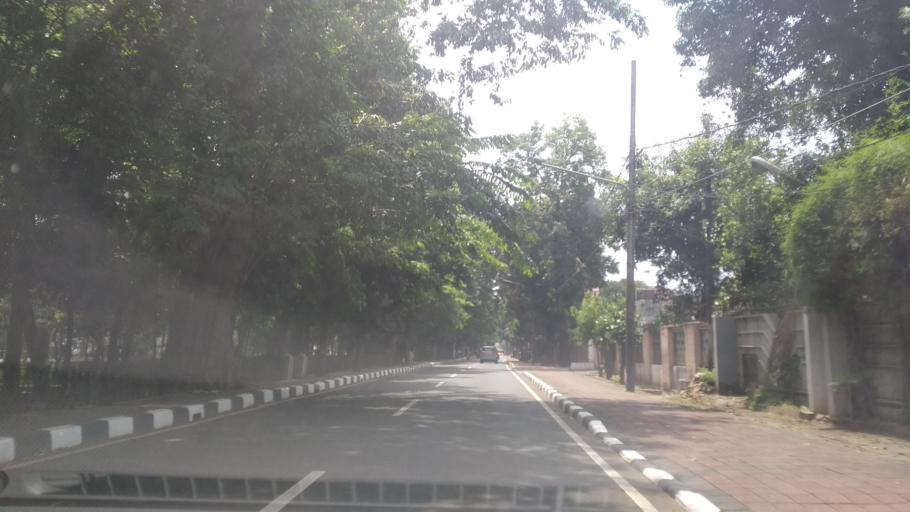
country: ID
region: Banten
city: South Tangerang
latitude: -6.2510
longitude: 106.7730
